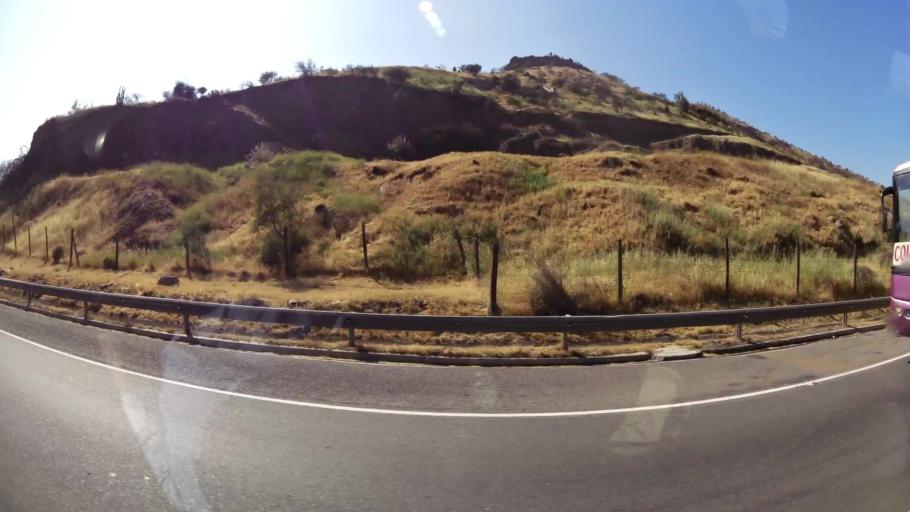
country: CL
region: Santiago Metropolitan
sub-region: Provincia de Chacabuco
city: Chicureo Abajo
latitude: -33.3189
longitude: -70.7068
